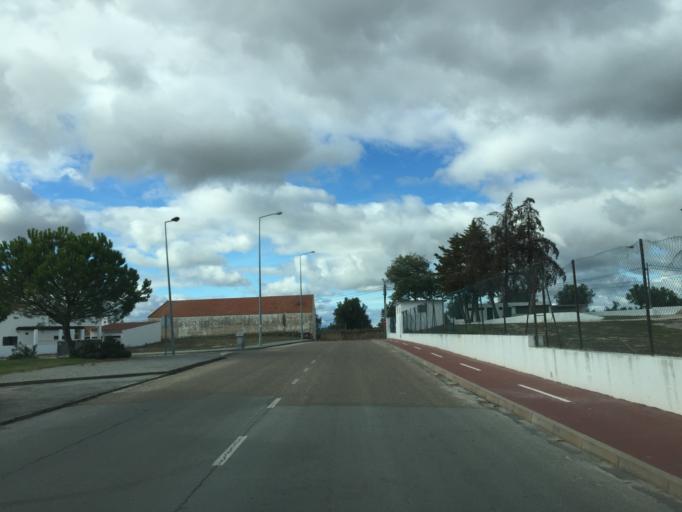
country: PT
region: Portalegre
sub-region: Alter do Chao
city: Alter do Chao
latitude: 39.1981
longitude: -7.6635
